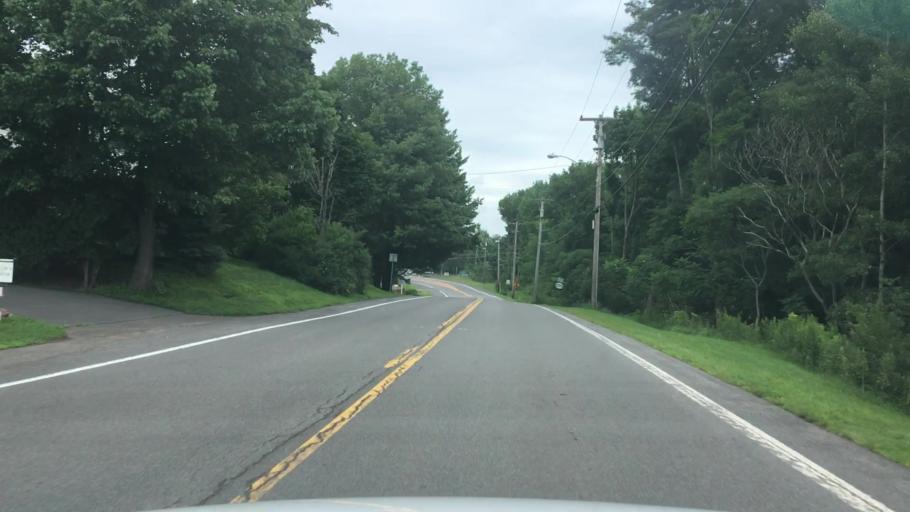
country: US
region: New York
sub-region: Otsego County
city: West End
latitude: 42.4404
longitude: -75.1105
